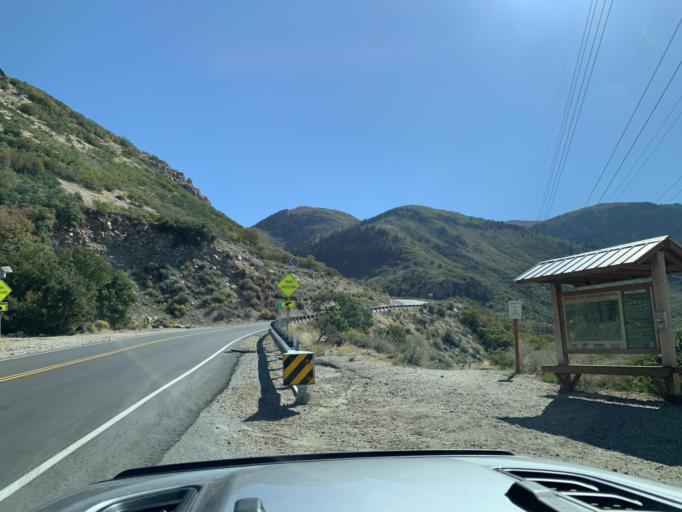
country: US
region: Utah
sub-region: Weber County
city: North Ogden
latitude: 41.3152
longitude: -111.9316
